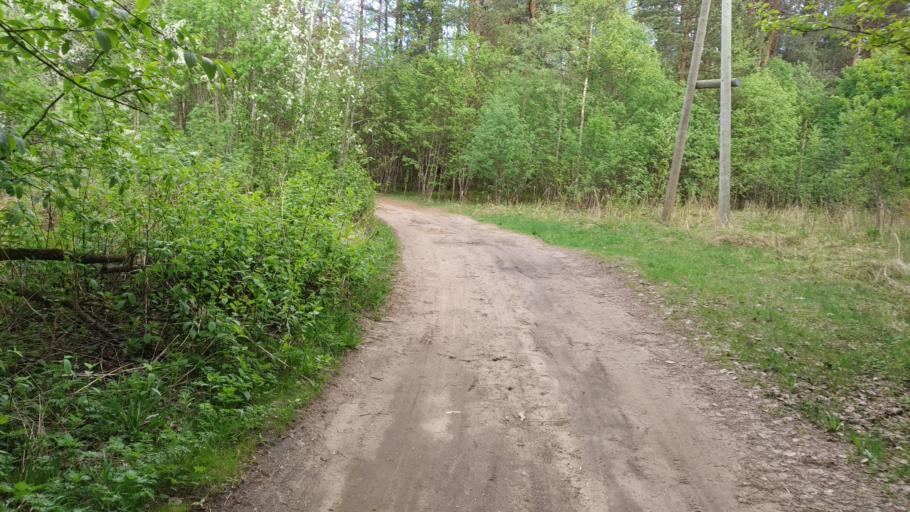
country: RU
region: Republic of Karelia
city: Sheltozero
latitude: 61.3781
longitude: 35.3615
